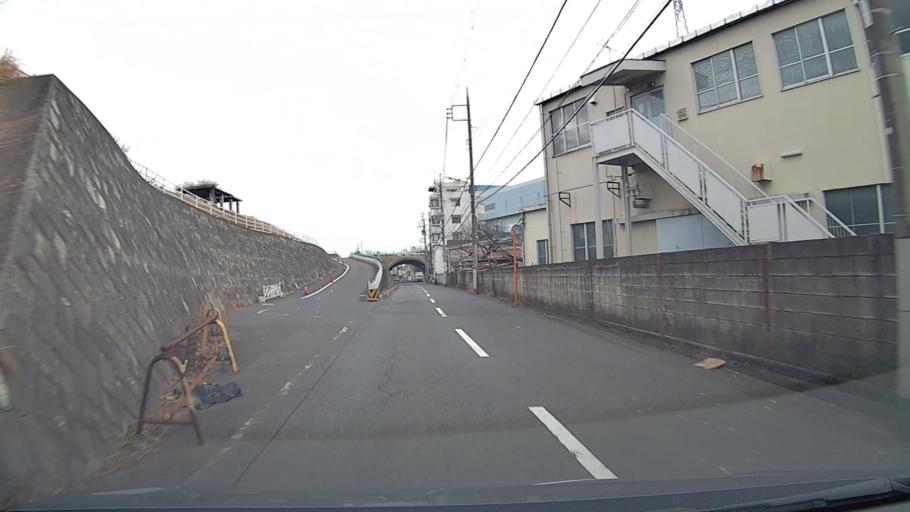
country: JP
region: Saitama
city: Shimotoda
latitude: 35.7963
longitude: 139.6742
